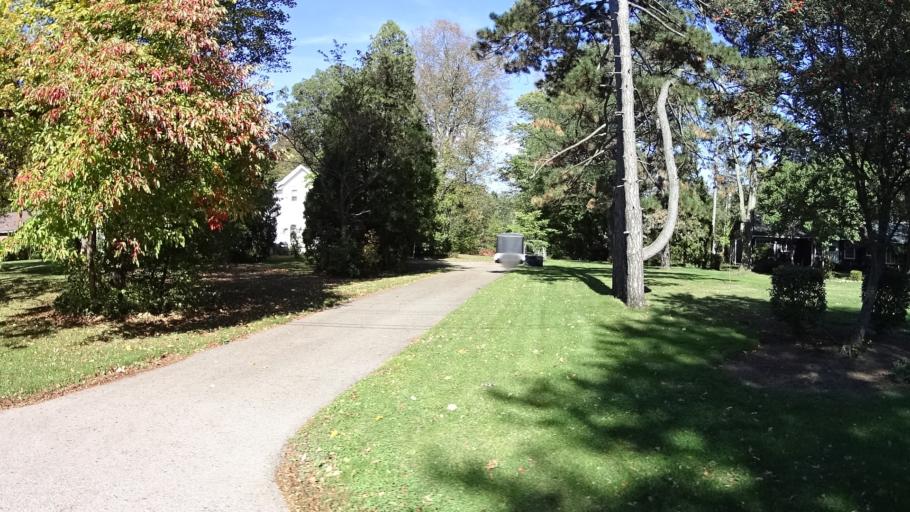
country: US
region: Ohio
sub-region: Lorain County
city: Amherst
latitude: 41.3915
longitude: -82.2252
